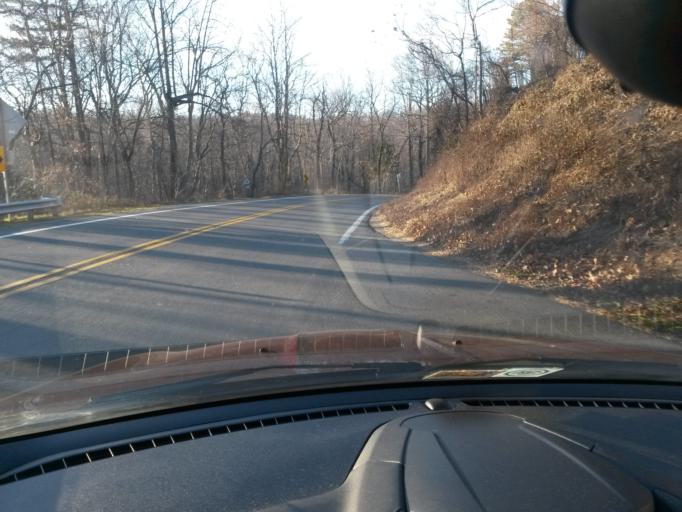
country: US
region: Virginia
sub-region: City of Buena Vista
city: Buena Vista
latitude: 37.7236
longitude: -79.2507
